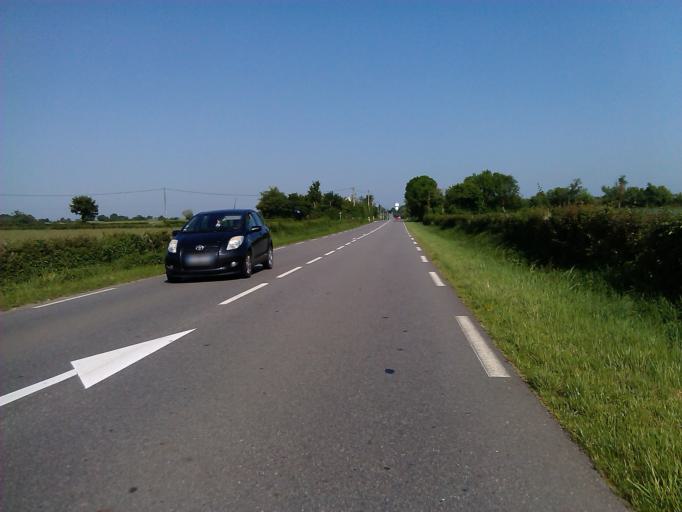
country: FR
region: Centre
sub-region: Departement de l'Indre
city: Neuvy-Saint-Sepulchre
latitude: 46.5832
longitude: 1.8338
